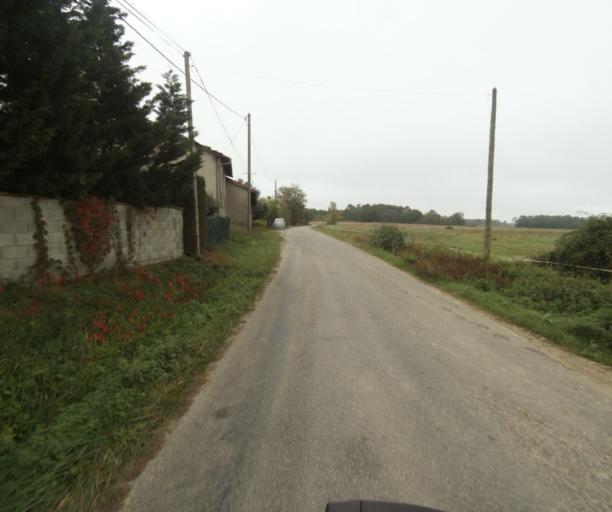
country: FR
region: Midi-Pyrenees
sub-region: Departement du Tarn-et-Garonne
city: Orgueil
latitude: 43.8984
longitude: 1.3946
